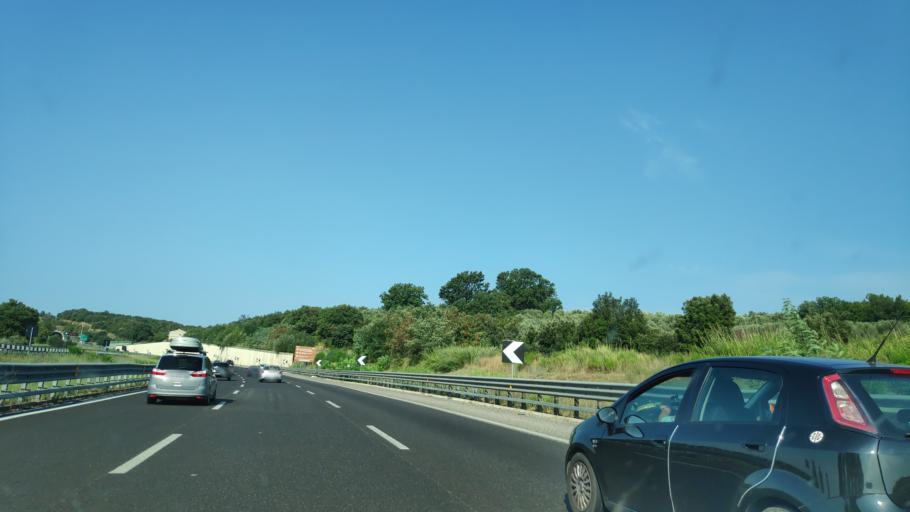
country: IT
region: Campania
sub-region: Provincia di Salerno
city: Quadrivio
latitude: 40.6135
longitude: 15.1435
